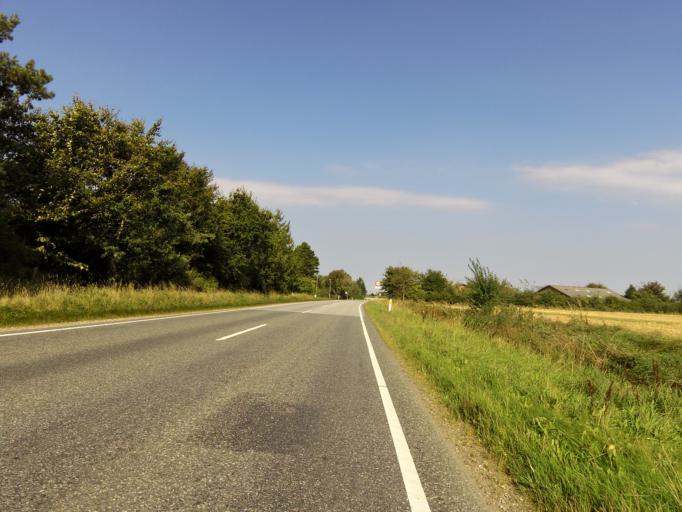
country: DK
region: South Denmark
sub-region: Vejen Kommune
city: Vejen
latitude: 55.4105
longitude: 9.1544
